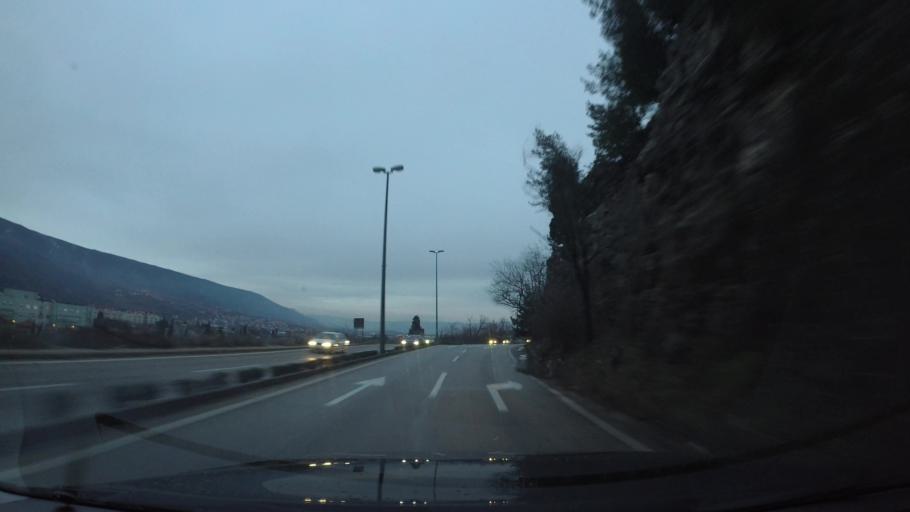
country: BA
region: Federation of Bosnia and Herzegovina
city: Rodoc
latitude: 43.3243
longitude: 17.8197
